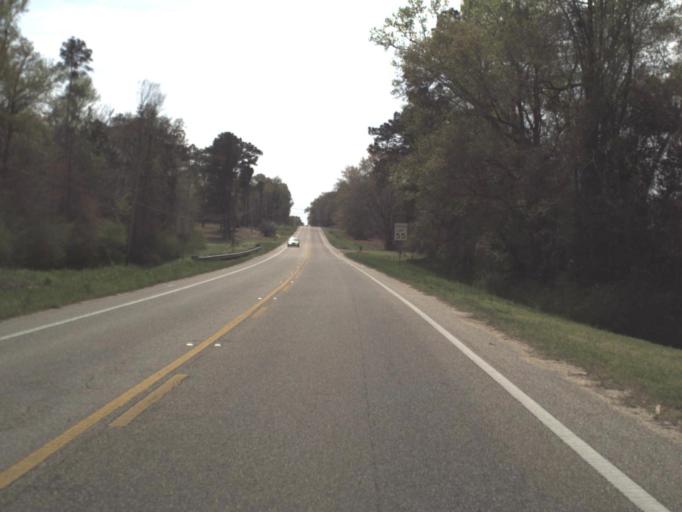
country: US
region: Florida
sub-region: Jackson County
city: Graceville
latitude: 30.9358
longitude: -85.5184
